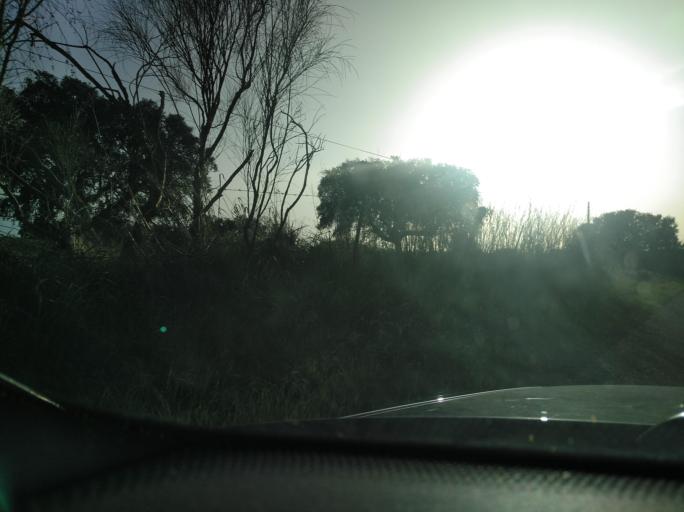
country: PT
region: Portalegre
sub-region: Campo Maior
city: Campo Maior
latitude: 39.0339
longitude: -6.9921
